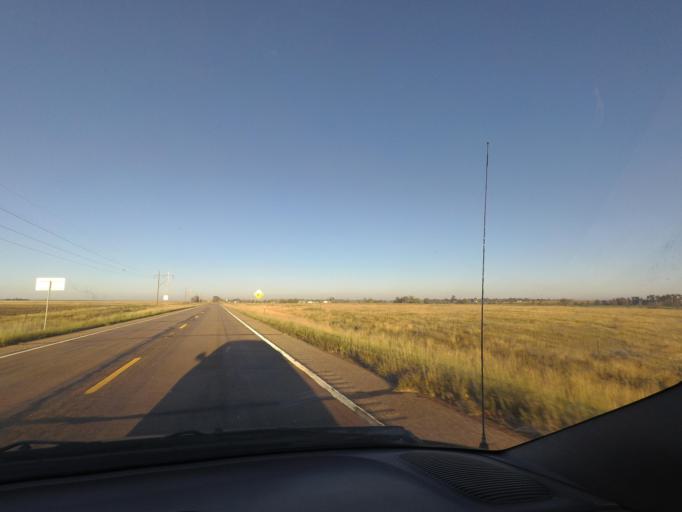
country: US
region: Colorado
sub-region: Yuma County
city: Yuma
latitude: 39.6553
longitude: -102.8378
